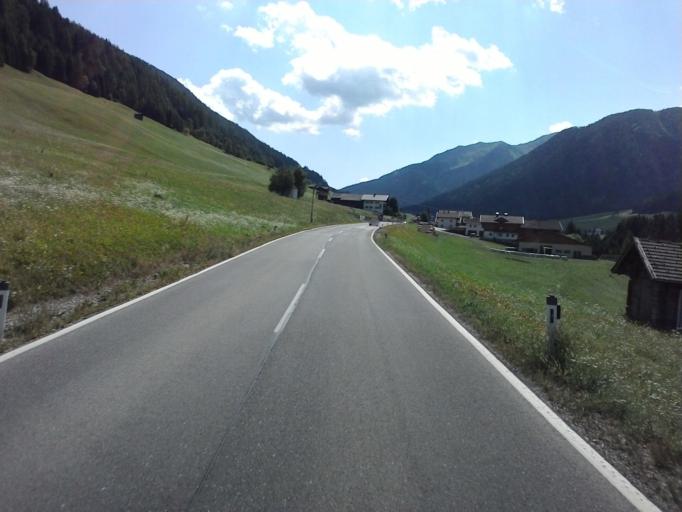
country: AT
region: Tyrol
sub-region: Politischer Bezirk Lienz
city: Kartitsch
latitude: 46.7332
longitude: 12.4835
